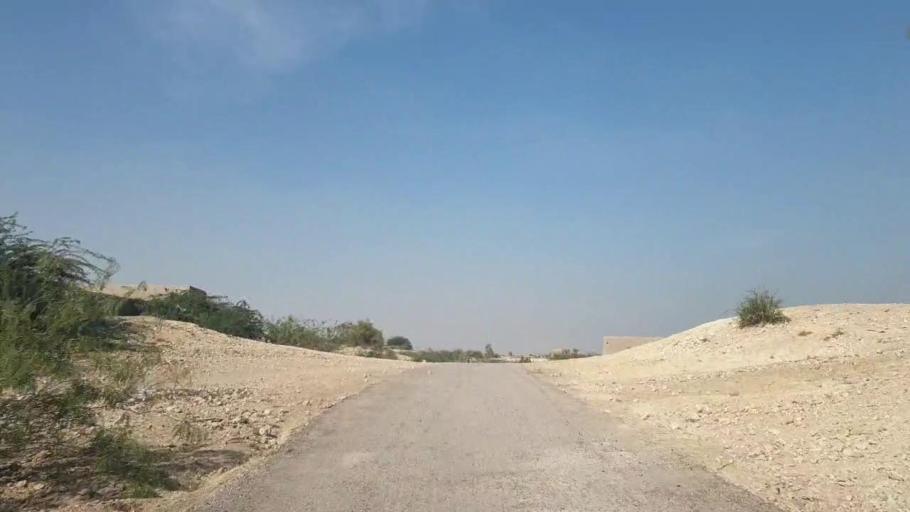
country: PK
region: Sindh
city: Hala
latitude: 25.7347
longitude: 68.2961
